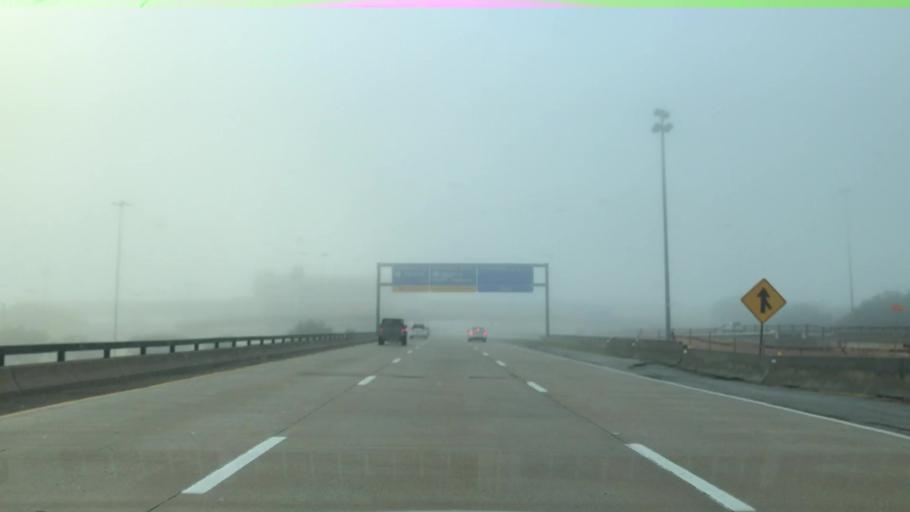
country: US
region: Texas
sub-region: Tarrant County
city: Grapevine
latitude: 32.9061
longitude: -97.0410
